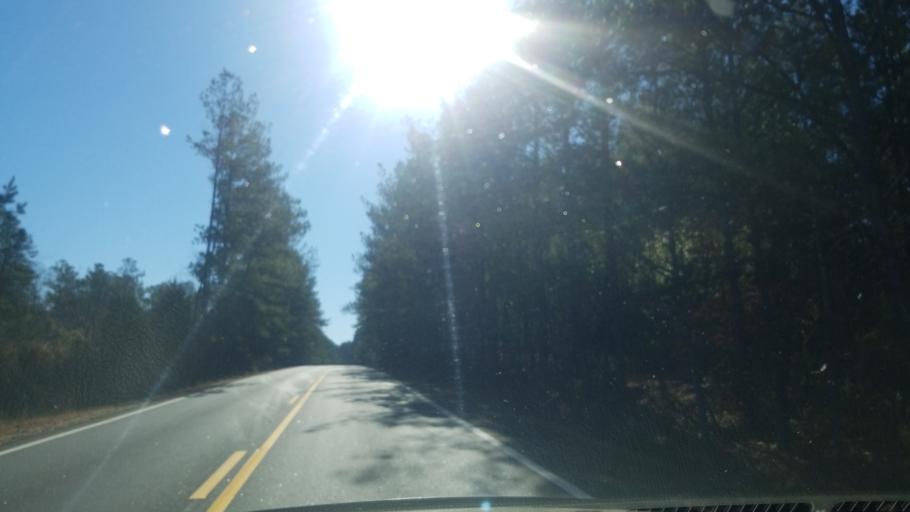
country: US
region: Alabama
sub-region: Chambers County
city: Valley
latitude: 32.8294
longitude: -85.1097
